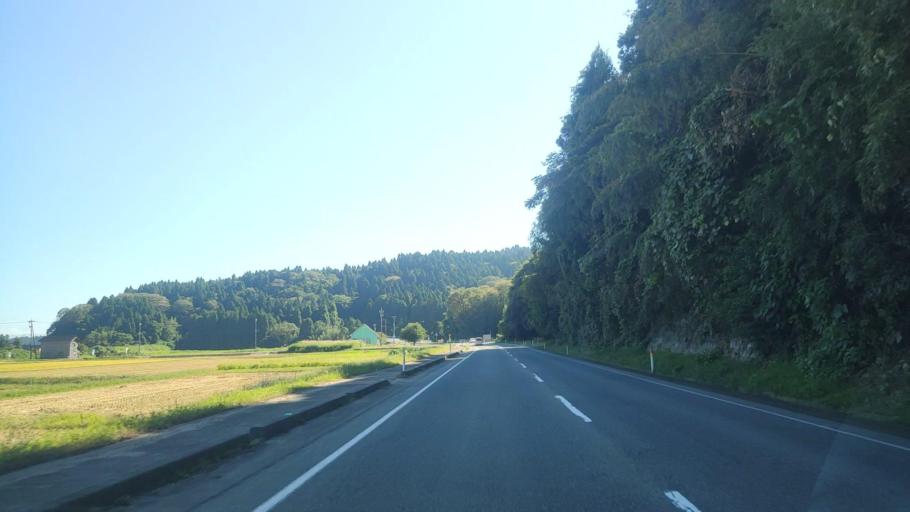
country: JP
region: Ishikawa
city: Nanao
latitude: 37.3888
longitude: 137.2333
